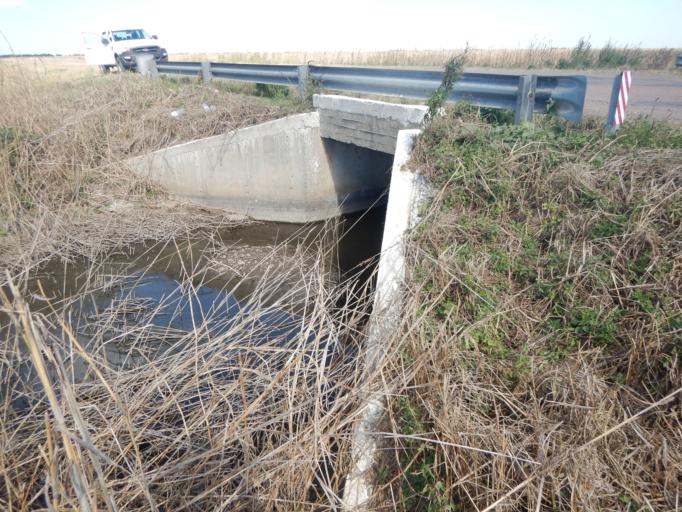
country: AR
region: Santa Fe
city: Tostado
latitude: -28.7103
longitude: -61.5380
